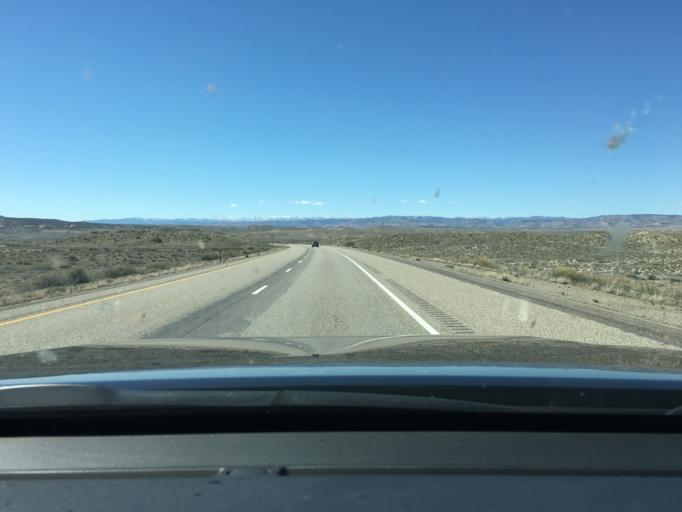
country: US
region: Colorado
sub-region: Mesa County
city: Loma
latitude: 39.1953
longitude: -109.0563
